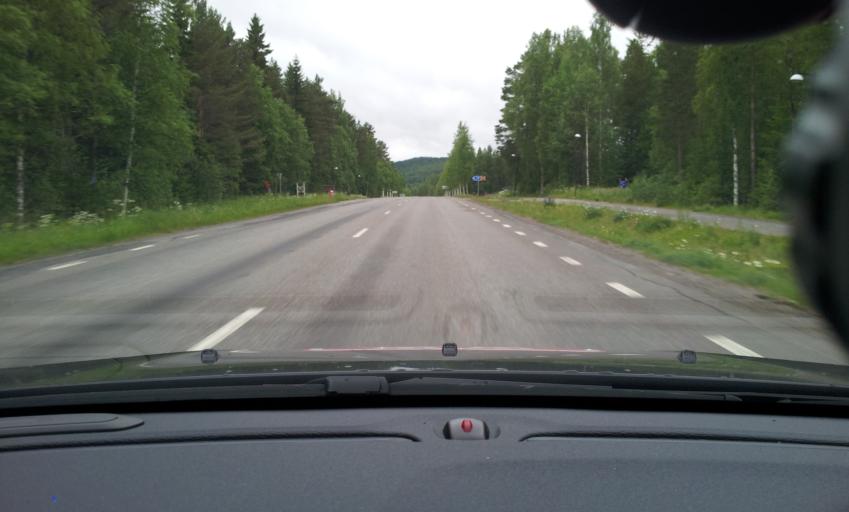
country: SE
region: Jaemtland
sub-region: Ragunda Kommun
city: Hammarstrand
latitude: 63.0171
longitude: 16.6496
